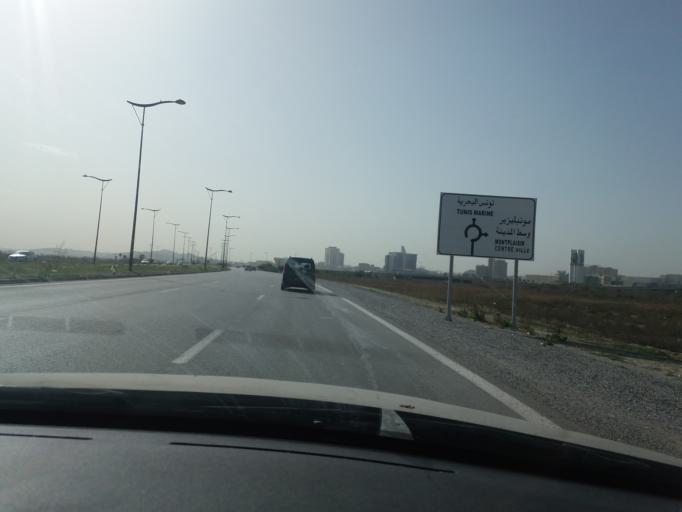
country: TN
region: Tunis
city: Tunis
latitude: 36.8162
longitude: 10.1955
